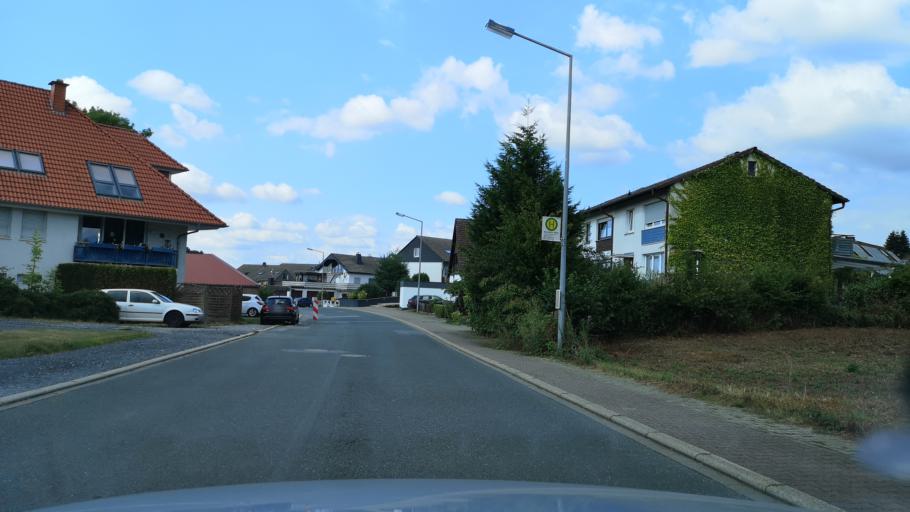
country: DE
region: North Rhine-Westphalia
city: Iserlohn
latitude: 51.4253
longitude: 7.7145
